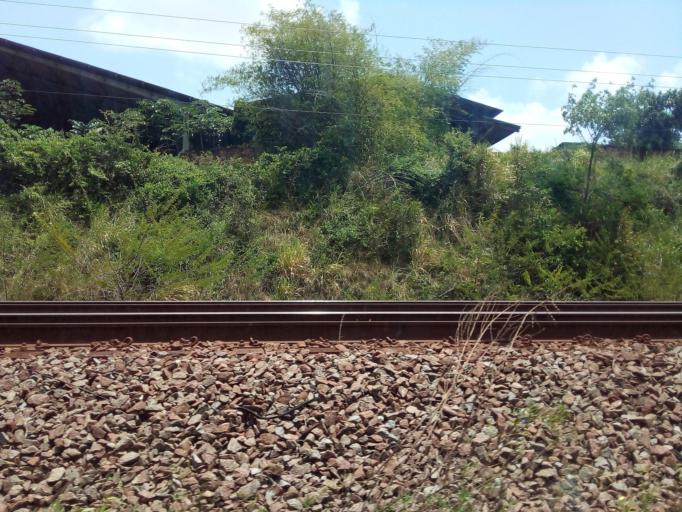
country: BR
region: Maranhao
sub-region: Sao Luis
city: Sao Luis
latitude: -2.7069
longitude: -44.3156
